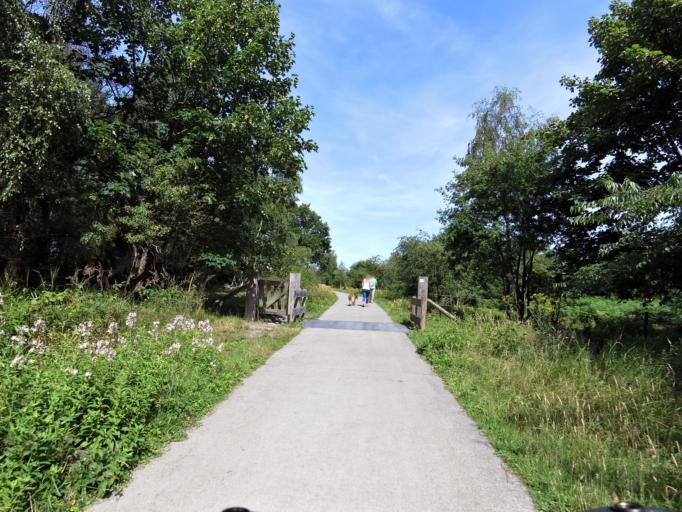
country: NL
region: Zeeland
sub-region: Schouwen-Duiveland
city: Burgh
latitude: 51.6845
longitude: 3.7085
